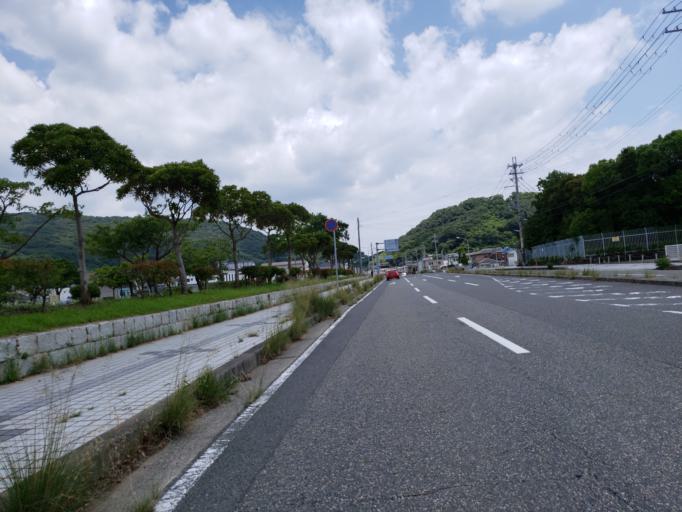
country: JP
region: Hyogo
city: Kariya
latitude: 34.7377
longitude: 134.4058
